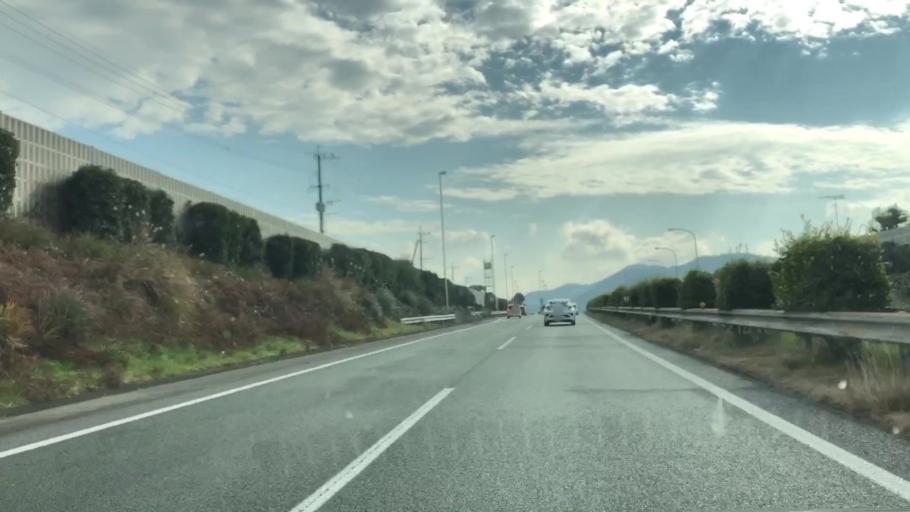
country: JP
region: Fukuoka
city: Setakamachi-takayanagi
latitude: 33.1314
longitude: 130.5173
